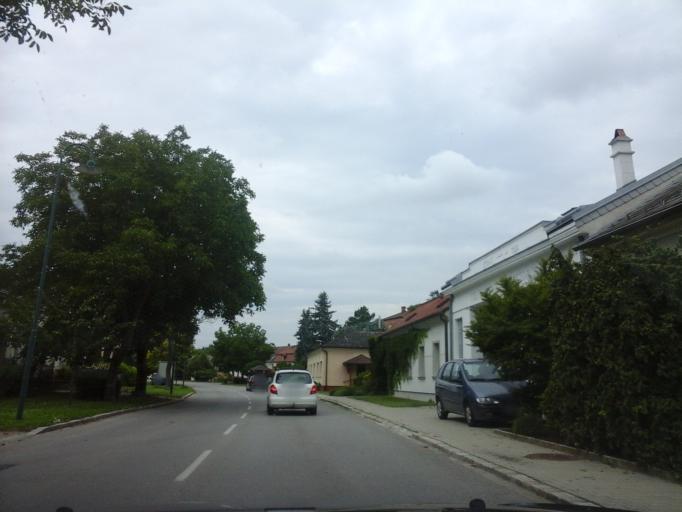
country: AT
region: Lower Austria
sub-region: Politischer Bezirk Ganserndorf
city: Haringsee
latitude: 48.1635
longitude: 16.7538
